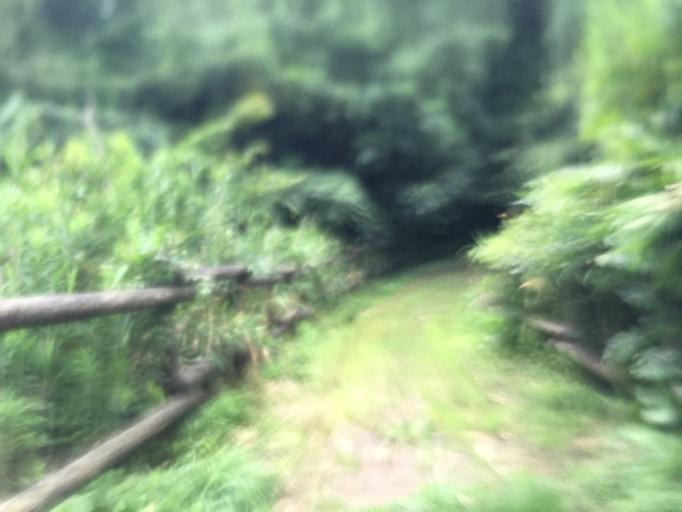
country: JP
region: Aichi
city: Ishiki
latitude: 34.7284
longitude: 137.0491
